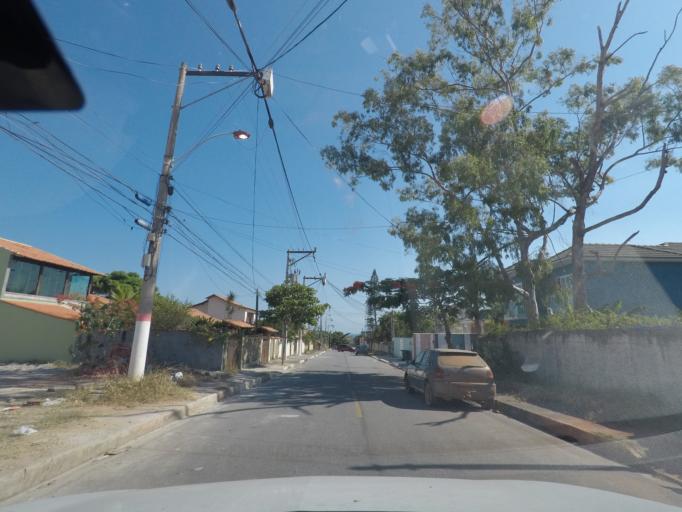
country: BR
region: Rio de Janeiro
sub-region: Niteroi
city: Niteroi
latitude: -22.9657
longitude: -42.9738
